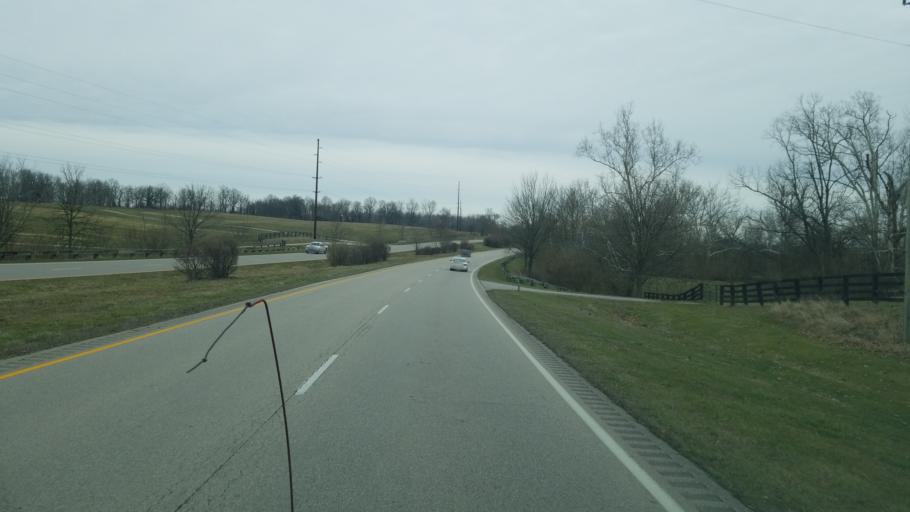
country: US
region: Kentucky
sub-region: Bourbon County
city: Paris
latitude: 38.1764
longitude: -84.3055
